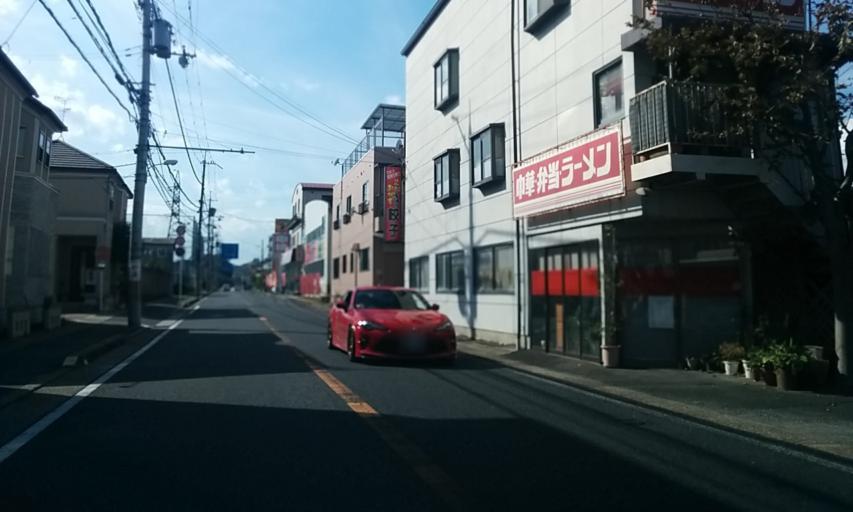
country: JP
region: Nara
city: Nara-shi
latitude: 34.7368
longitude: 135.8071
